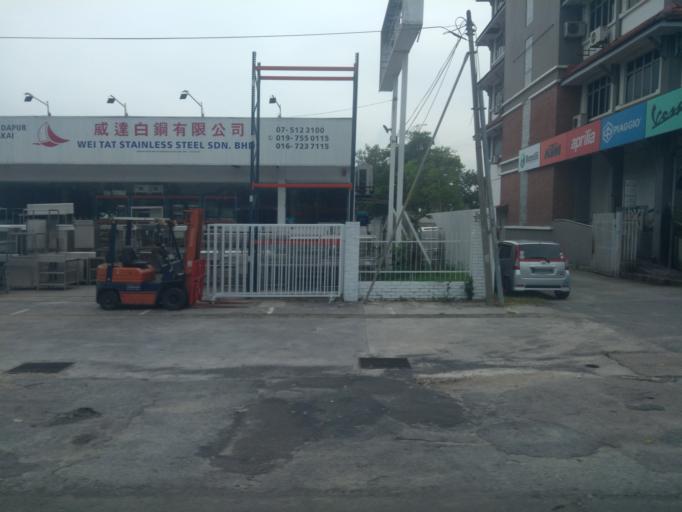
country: MY
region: Johor
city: Johor Bahru
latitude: 1.4883
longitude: 103.7132
